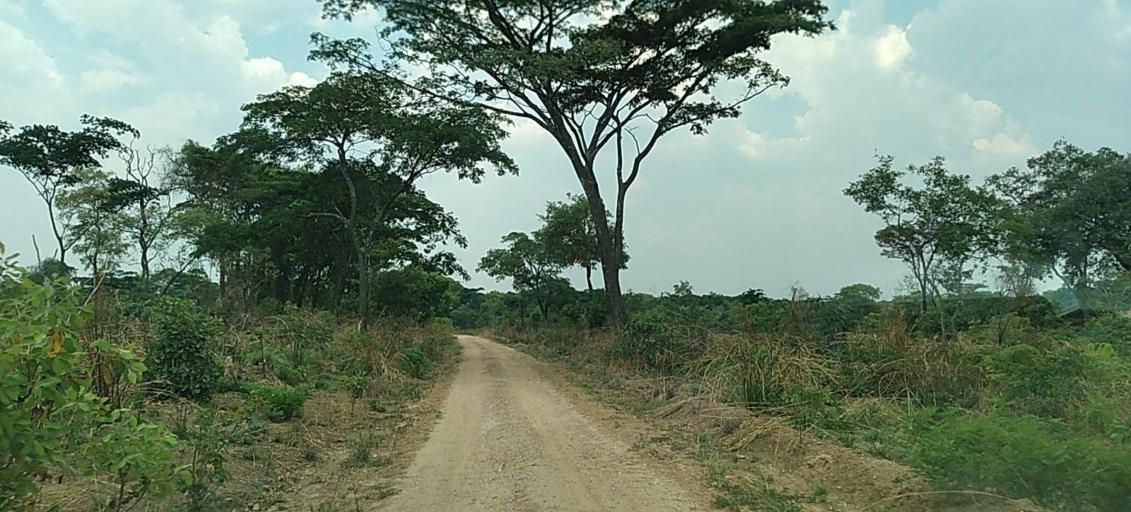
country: ZM
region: Copperbelt
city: Chingola
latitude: -12.7539
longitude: 27.7206
